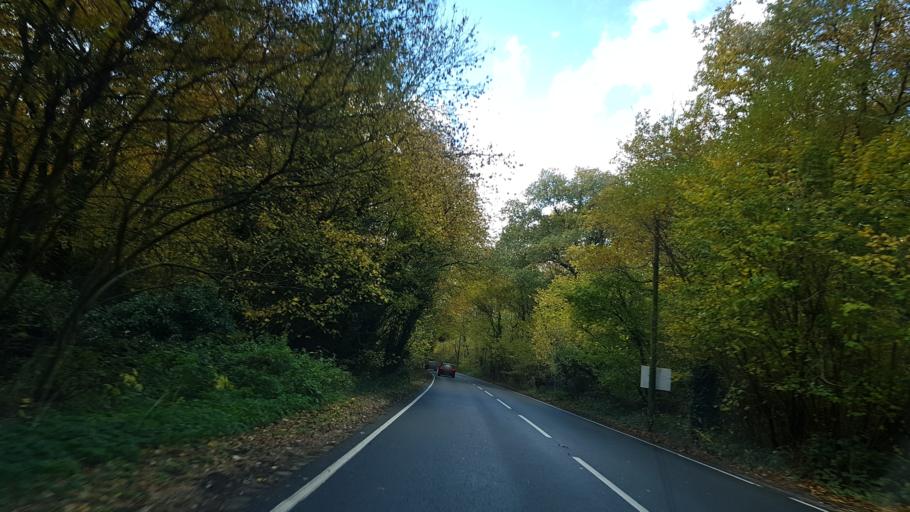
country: GB
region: England
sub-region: Surrey
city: Haslemere
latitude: 51.1126
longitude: -0.6832
